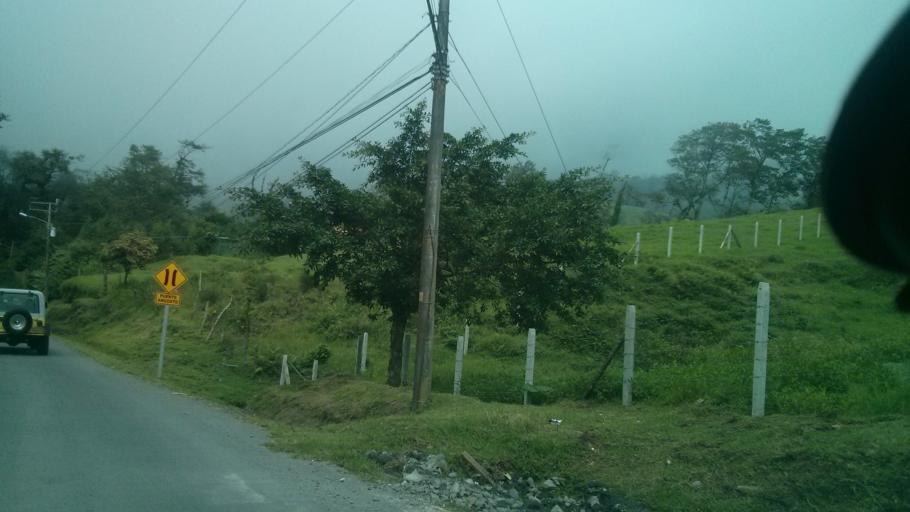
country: CR
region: San Jose
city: Ipis
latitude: 9.9995
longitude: -83.9585
